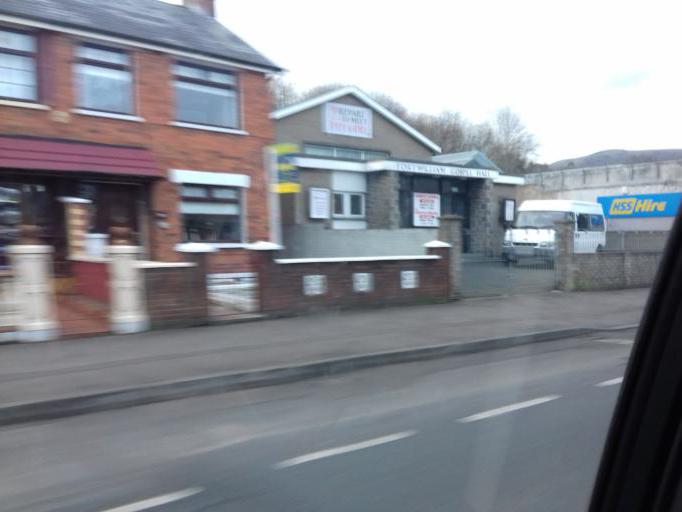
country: GB
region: Northern Ireland
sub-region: Newtownabbey District
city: Newtownabbey
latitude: 54.6260
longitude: -5.9235
